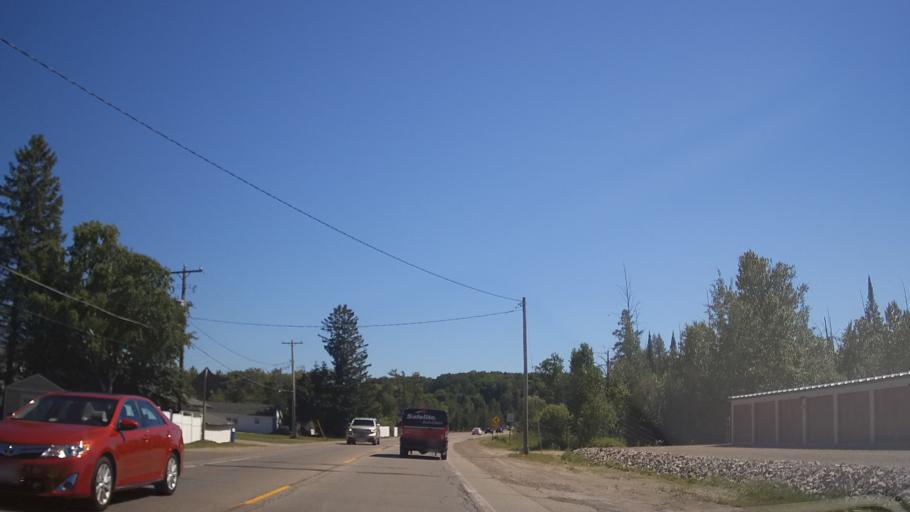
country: US
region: Michigan
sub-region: Emmet County
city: Petoskey
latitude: 45.4151
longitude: -84.8654
